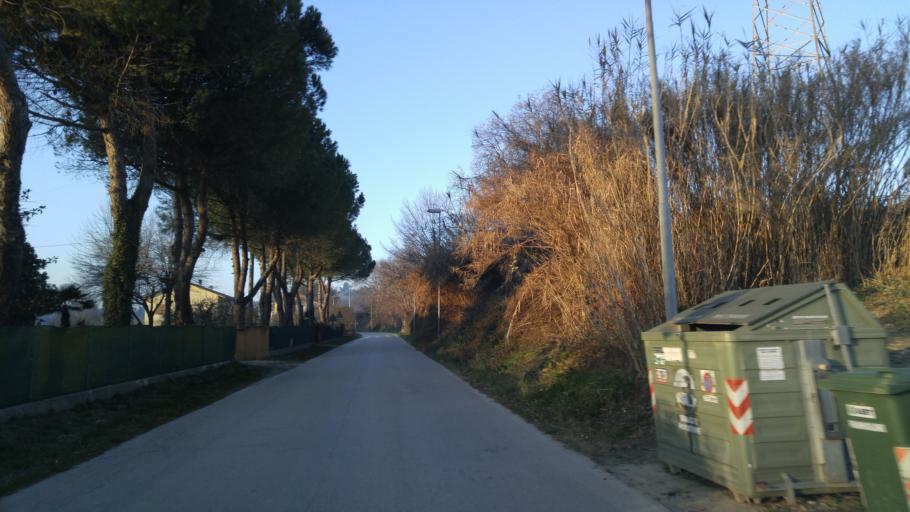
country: IT
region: The Marches
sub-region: Provincia di Pesaro e Urbino
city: Fenile
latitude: 43.8477
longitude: 12.9681
